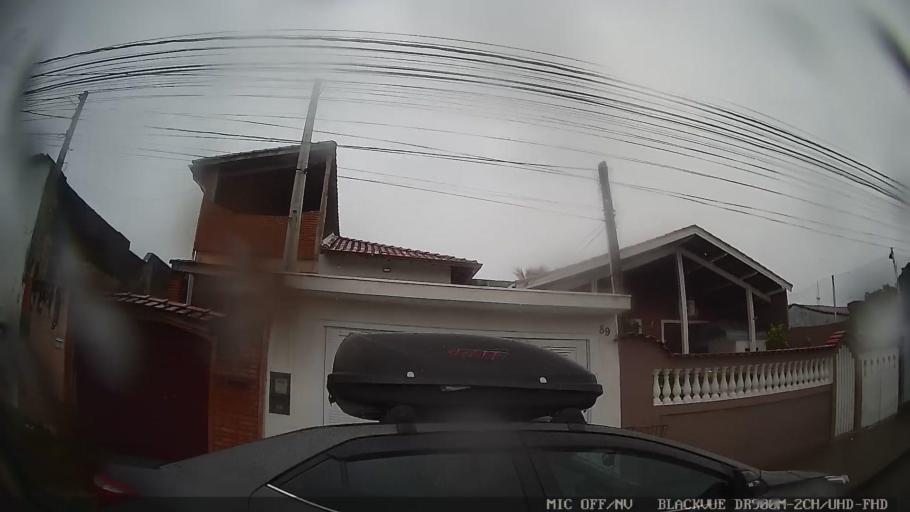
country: BR
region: Sao Paulo
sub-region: Itanhaem
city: Itanhaem
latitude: -24.1887
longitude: -46.8174
